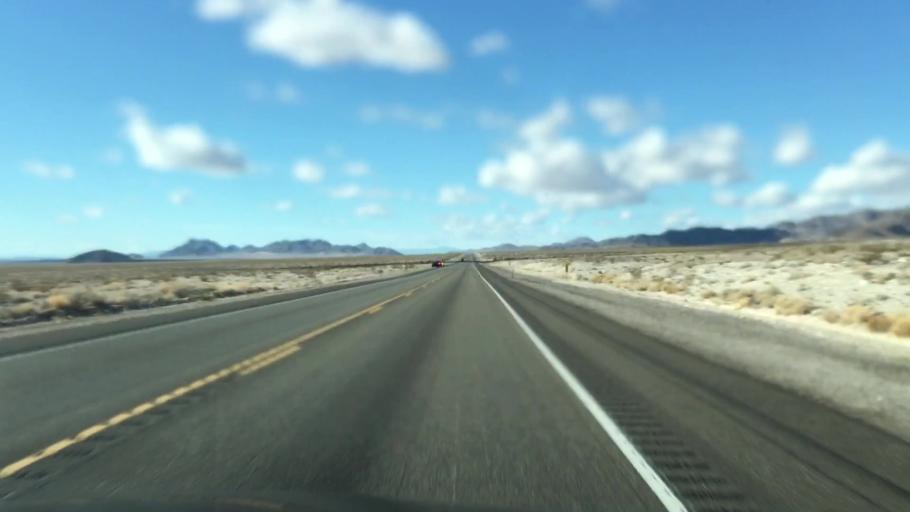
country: US
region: Nevada
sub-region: Nye County
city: Pahrump
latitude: 36.5877
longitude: -116.2178
